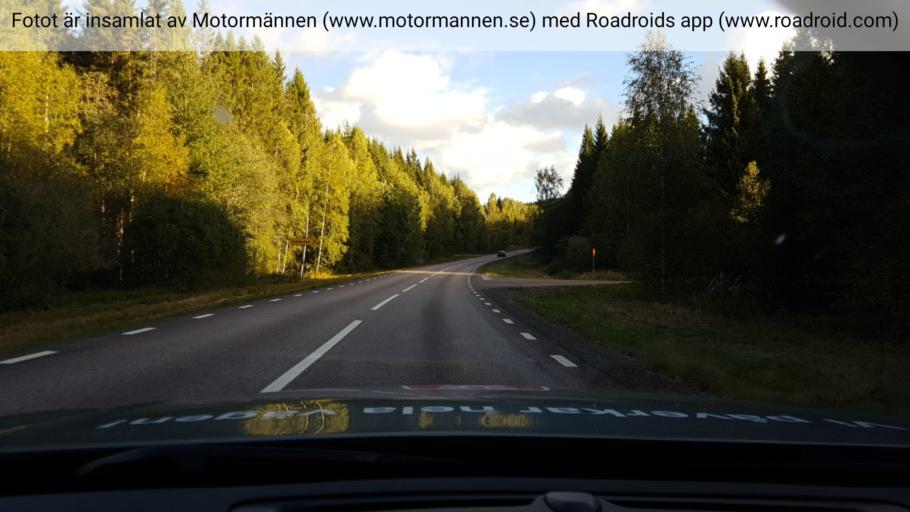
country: SE
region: Vaermland
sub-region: Karlstads Kommun
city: Molkom
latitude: 59.6613
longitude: 13.7066
